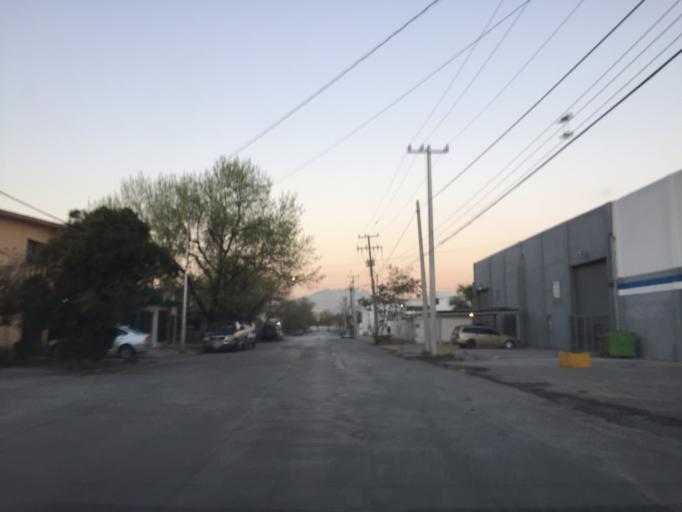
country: MX
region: Nuevo Leon
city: Guadalupe
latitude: 25.6994
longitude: -100.2200
